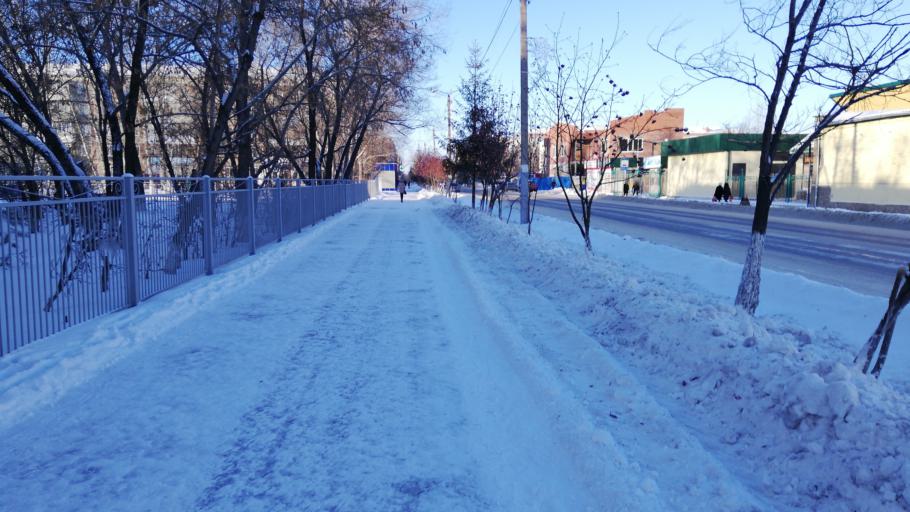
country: KZ
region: Soltustik Qazaqstan
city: Petropavlovsk
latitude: 54.8634
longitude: 69.1458
